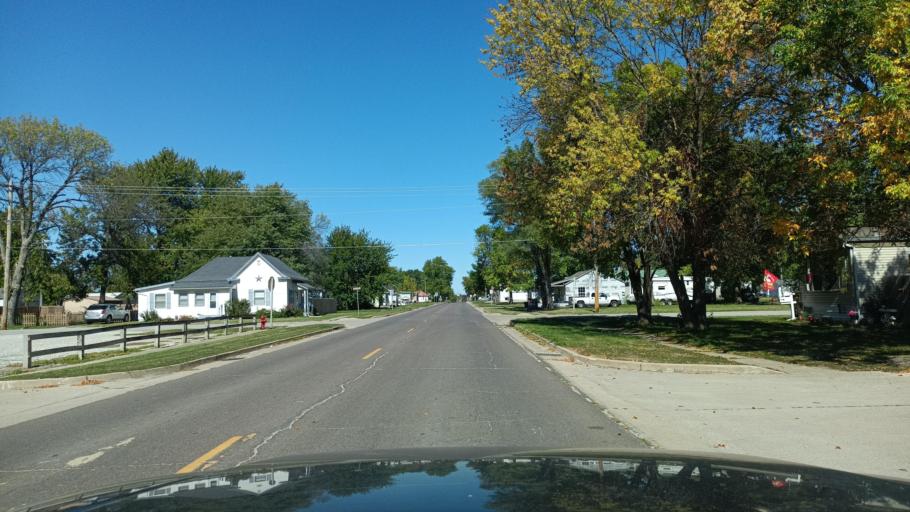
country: US
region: Missouri
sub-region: Macon County
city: La Plata
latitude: 40.0240
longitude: -92.4886
